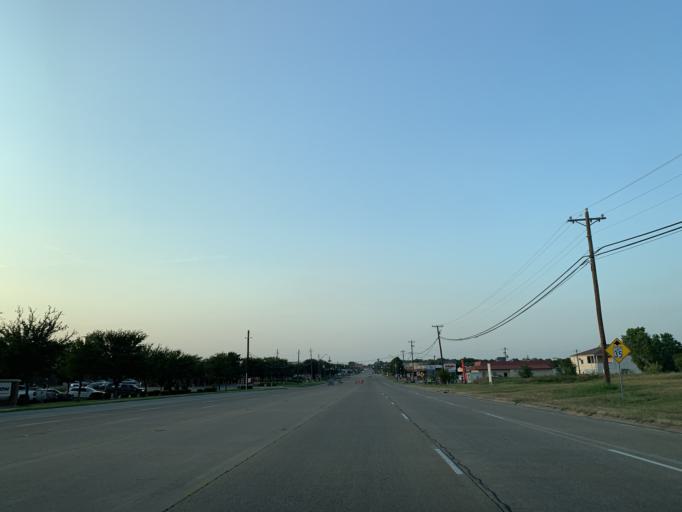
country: US
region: Texas
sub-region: Tarrant County
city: Keller
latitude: 32.9241
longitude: -97.2542
